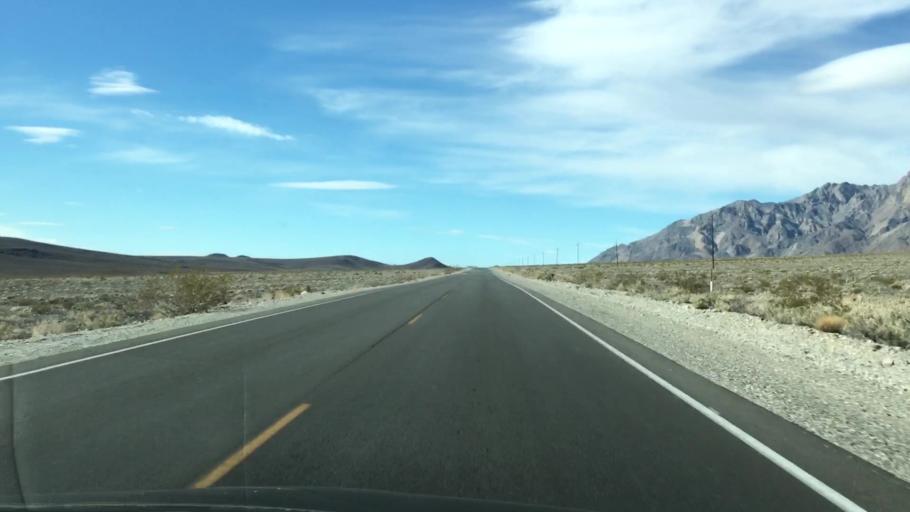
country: US
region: Nevada
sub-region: Nye County
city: Pahrump
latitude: 36.3258
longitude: -116.5649
